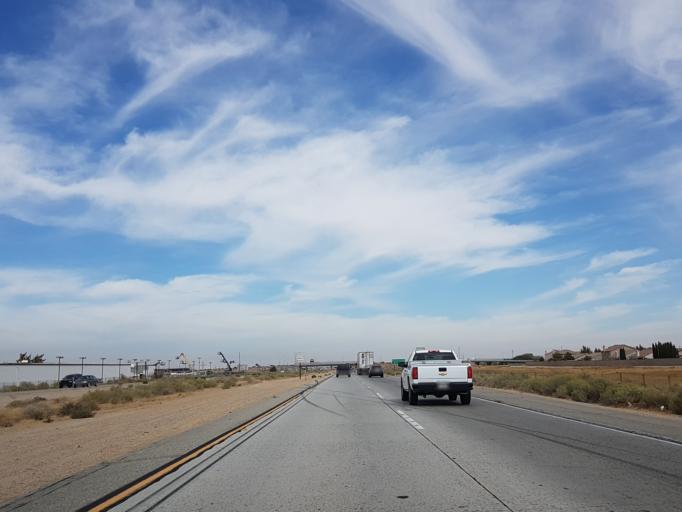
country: US
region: California
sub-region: Los Angeles County
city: Lancaster
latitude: 34.7109
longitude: -118.1698
